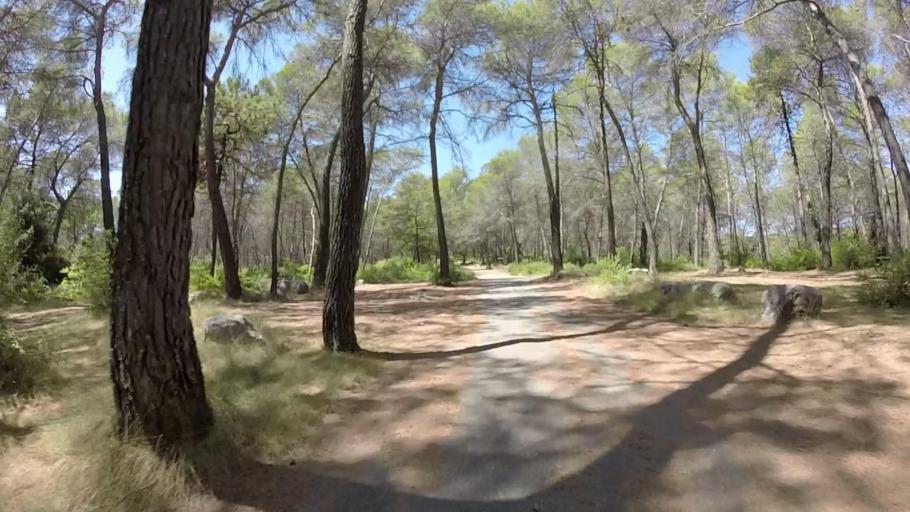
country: FR
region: Provence-Alpes-Cote d'Azur
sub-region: Departement des Alpes-Maritimes
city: Vallauris
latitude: 43.6086
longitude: 7.0483
